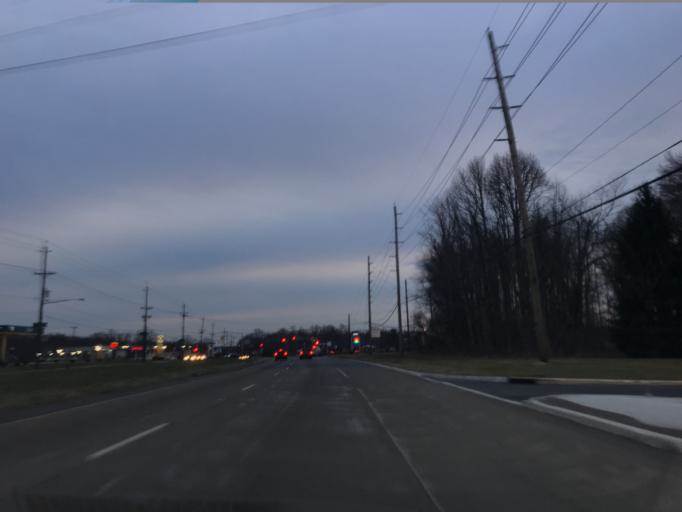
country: US
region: New Jersey
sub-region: Middlesex County
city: Dayton
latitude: 40.4130
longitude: -74.5051
